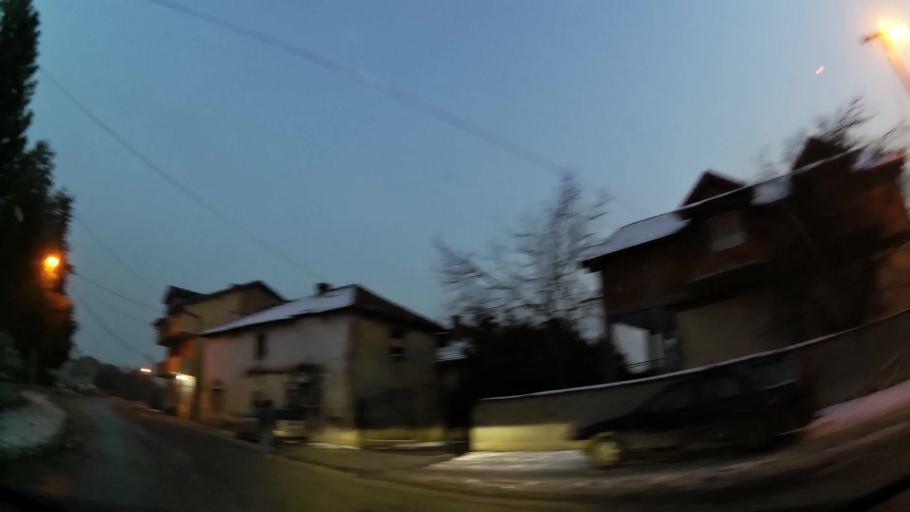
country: MK
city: Creshevo
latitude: 42.0038
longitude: 21.5165
